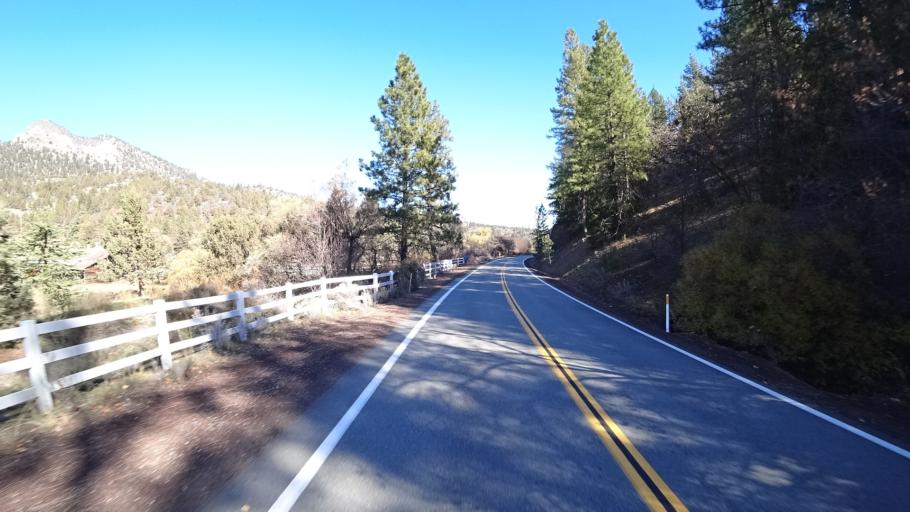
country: US
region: California
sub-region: Siskiyou County
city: Weed
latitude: 41.4624
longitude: -122.6213
